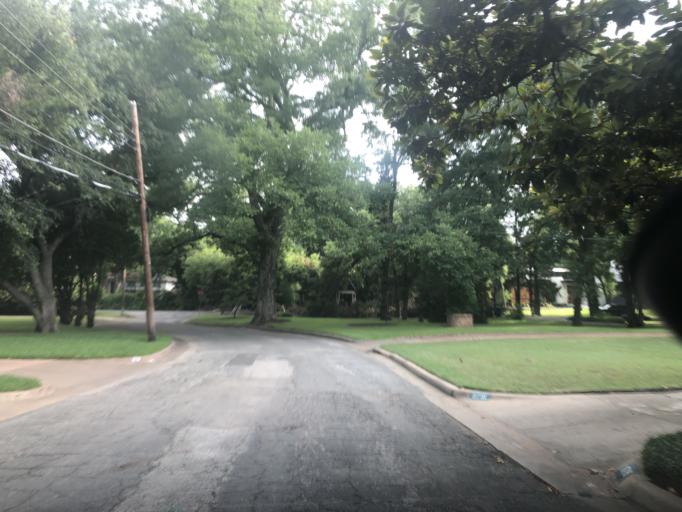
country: US
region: Texas
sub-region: Dallas County
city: University Park
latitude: 32.8577
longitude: -96.8417
